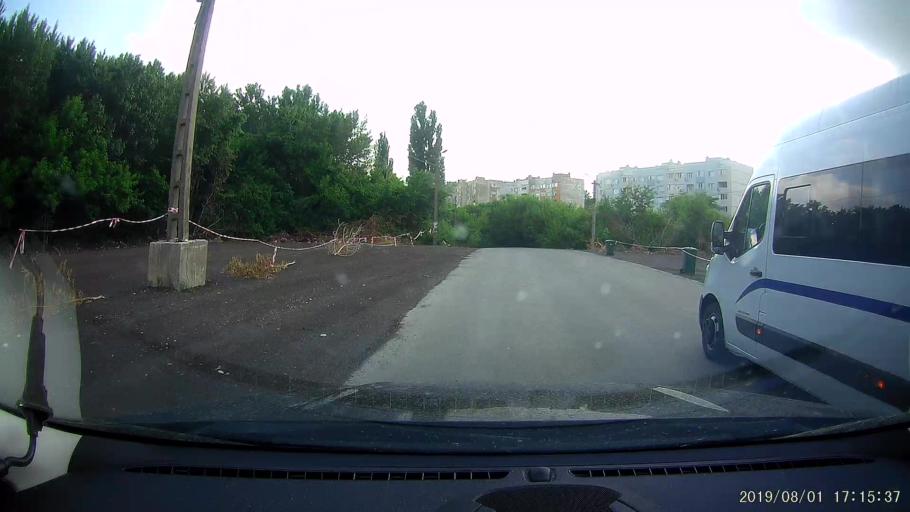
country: BG
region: Silistra
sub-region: Obshtina Silistra
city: Silistra
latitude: 44.1206
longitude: 27.2777
